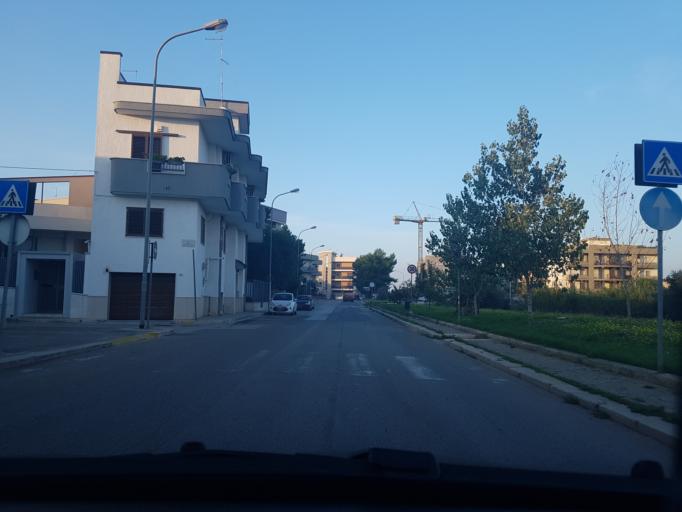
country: IT
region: Apulia
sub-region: Provincia di Bari
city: Bitritto
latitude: 41.0429
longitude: 16.8305
